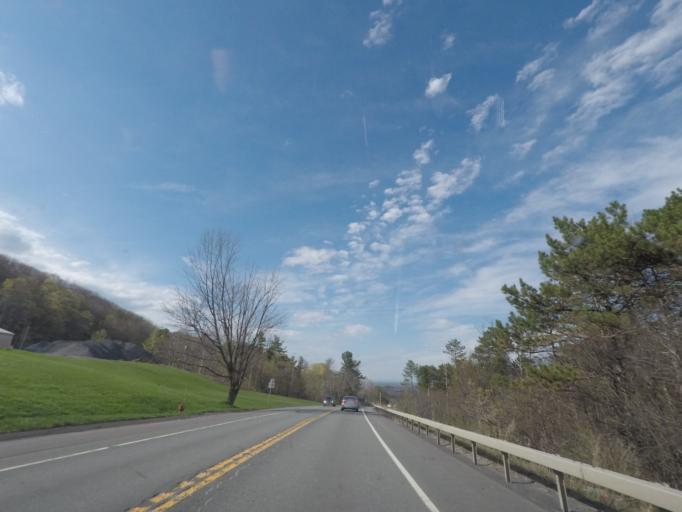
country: US
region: New York
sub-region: Albany County
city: Voorheesville
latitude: 42.6173
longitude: -73.9756
